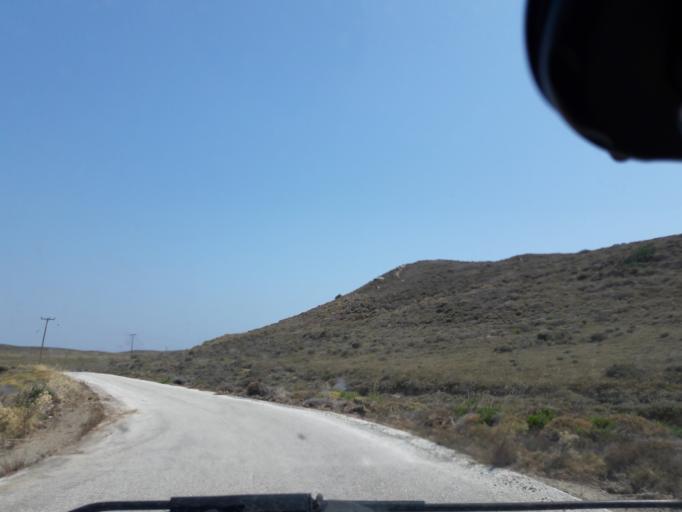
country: GR
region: North Aegean
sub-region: Nomos Lesvou
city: Myrina
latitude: 39.9750
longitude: 25.3526
